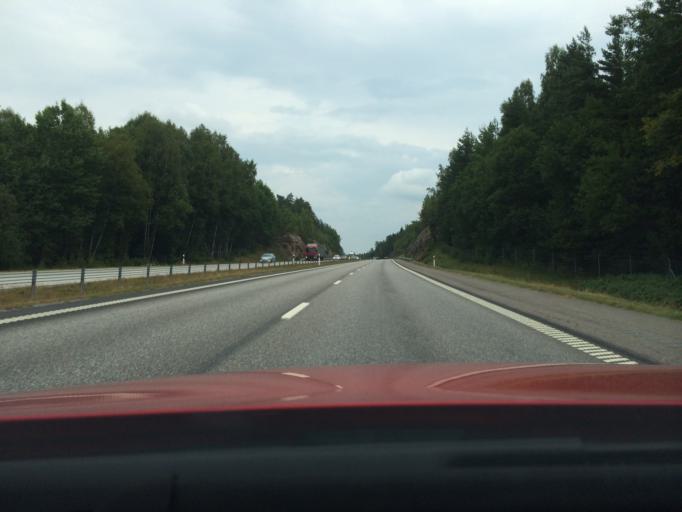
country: SE
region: OEstergoetland
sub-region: Norrkopings Kommun
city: Krokek
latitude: 58.7051
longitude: 16.3478
